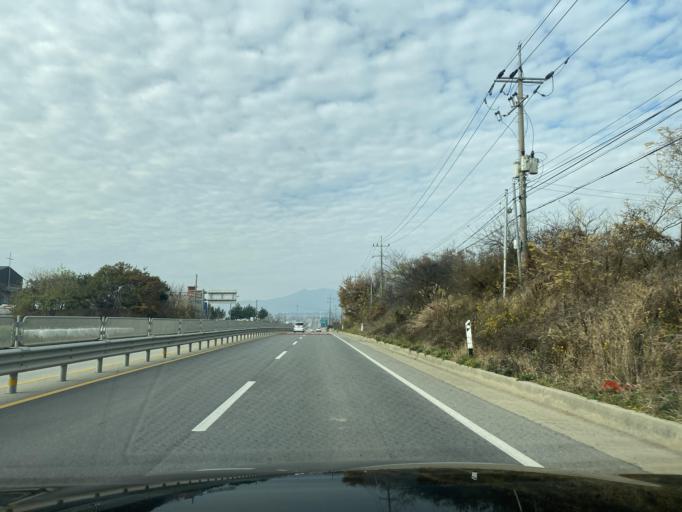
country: KR
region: Chungcheongnam-do
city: Yesan
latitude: 36.6903
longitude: 126.7476
